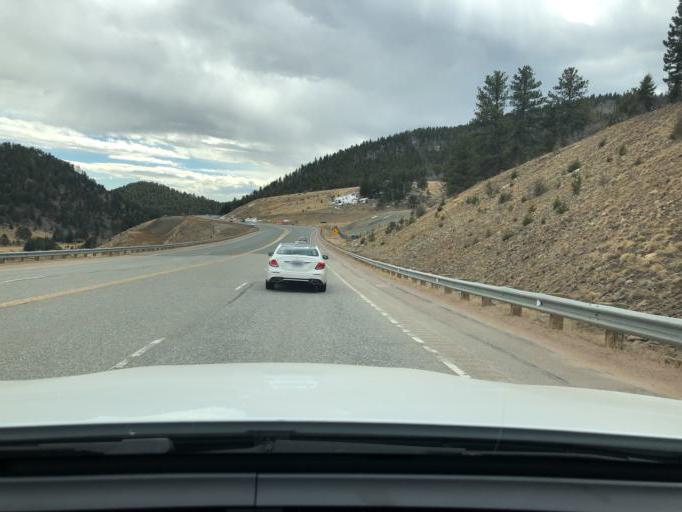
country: US
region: Colorado
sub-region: Gilpin County
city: Central City
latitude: 39.7816
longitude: -105.4826
